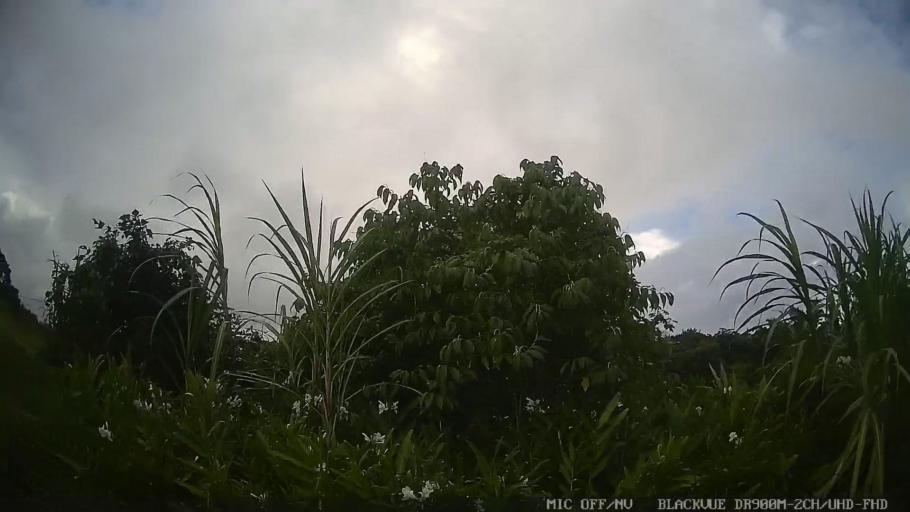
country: BR
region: Sao Paulo
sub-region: Itanhaem
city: Itanhaem
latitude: -24.2143
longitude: -46.8543
